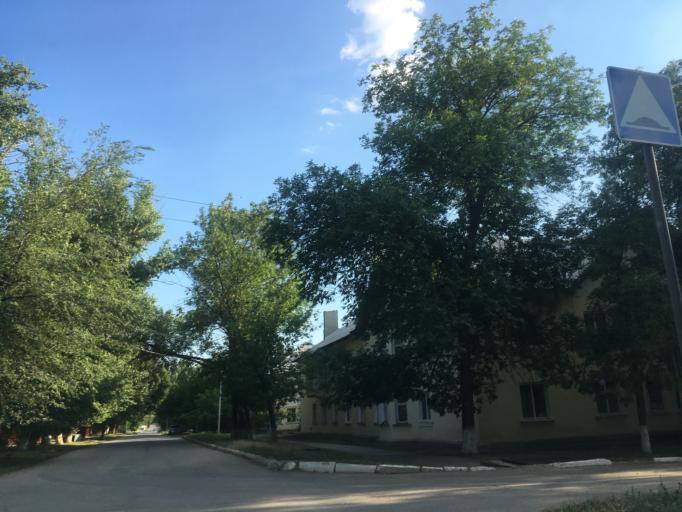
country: RU
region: Rostov
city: Masalovka
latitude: 48.4031
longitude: 40.2781
